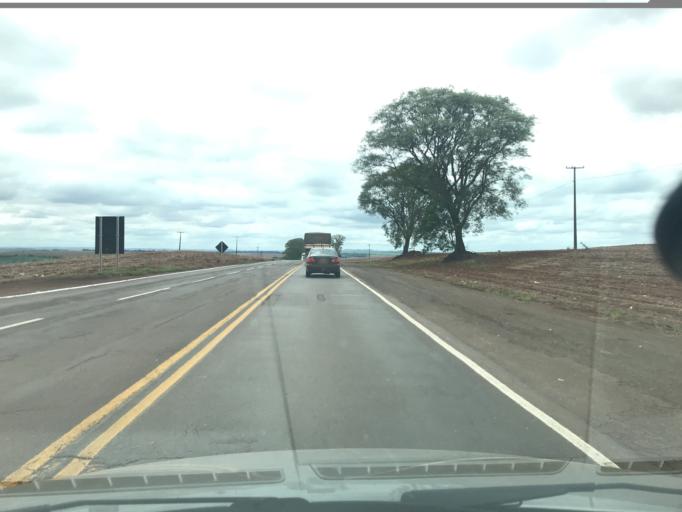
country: BR
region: Parana
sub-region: Terra Boa
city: Terra Boa
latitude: -23.6045
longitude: -52.4119
